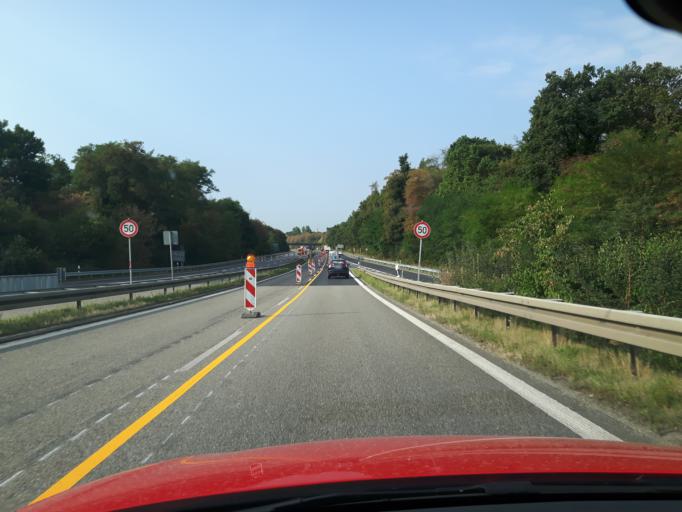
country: DE
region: Baden-Wuerttemberg
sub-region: Karlsruhe Region
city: Ettlingen
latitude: 48.9590
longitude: 8.3792
